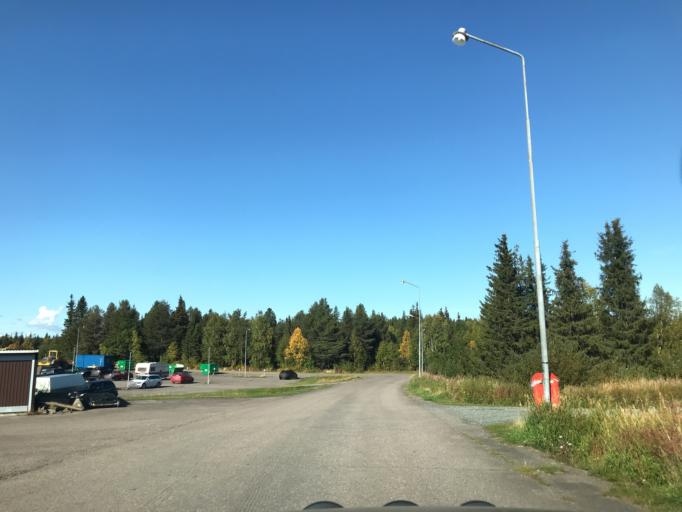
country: SE
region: Norrbotten
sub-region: Gallivare Kommun
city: Malmberget
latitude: 67.6497
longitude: 21.0592
